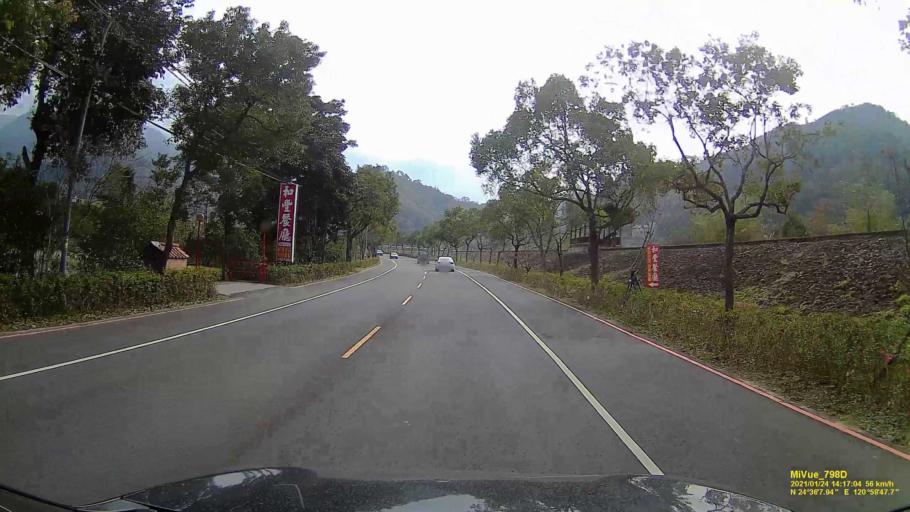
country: TW
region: Taiwan
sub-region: Miaoli
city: Miaoli
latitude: 24.6020
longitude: 120.9966
